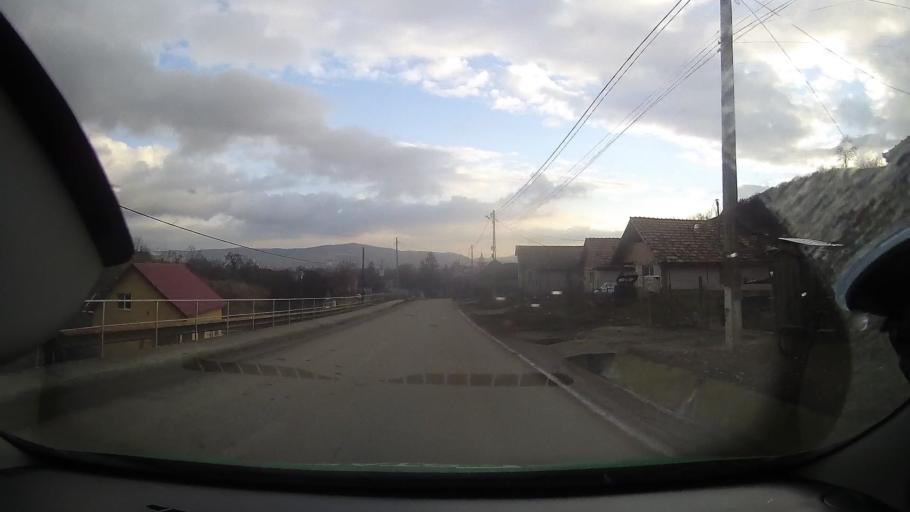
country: RO
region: Alba
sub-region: Comuna Lunca Muresului
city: Lunca Muresului
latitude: 46.4313
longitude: 23.9089
